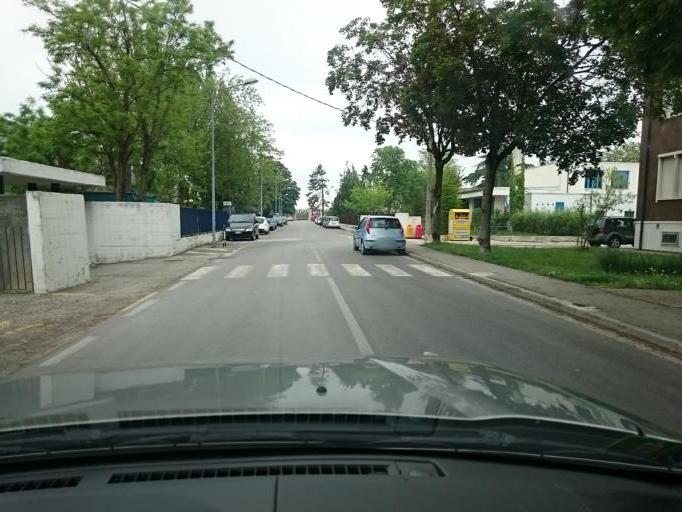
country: IT
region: Veneto
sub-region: Provincia di Padova
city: Correzzola
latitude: 45.2357
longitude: 12.0664
